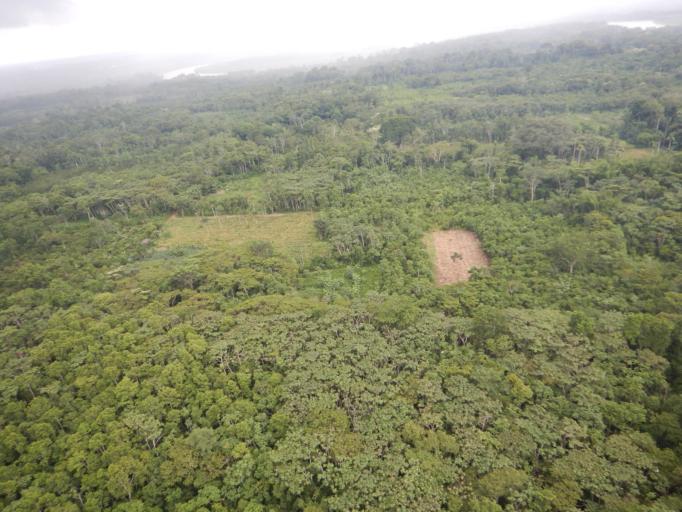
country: BO
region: Cochabamba
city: Chimore
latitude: -17.0649
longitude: -64.7925
